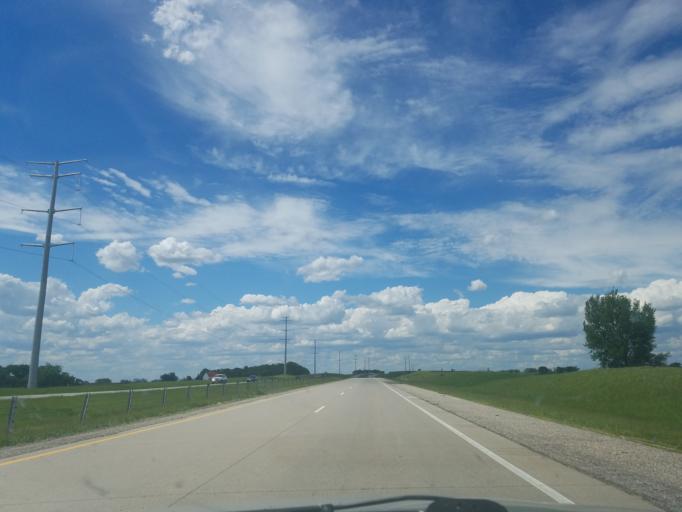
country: US
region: Minnesota
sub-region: Otter Tail County
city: Pelican Rapids
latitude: 46.4546
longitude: -96.2491
